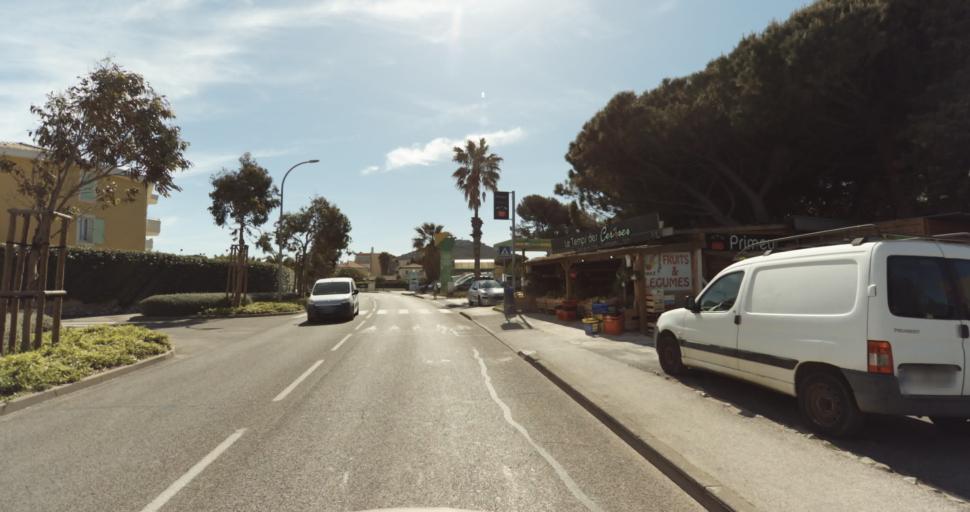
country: FR
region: Provence-Alpes-Cote d'Azur
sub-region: Departement du Var
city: Sanary-sur-Mer
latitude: 43.1076
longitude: 5.8173
